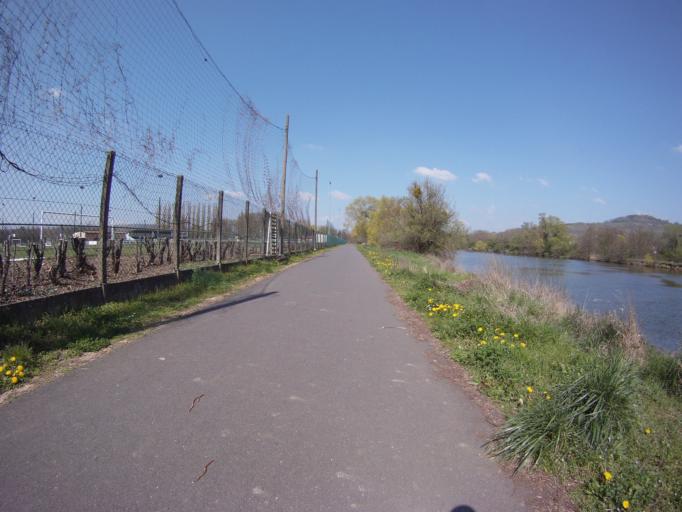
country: FR
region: Lorraine
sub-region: Departement de Meurthe-et-Moselle
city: Pont-a-Mousson
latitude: 48.8945
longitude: 6.0600
